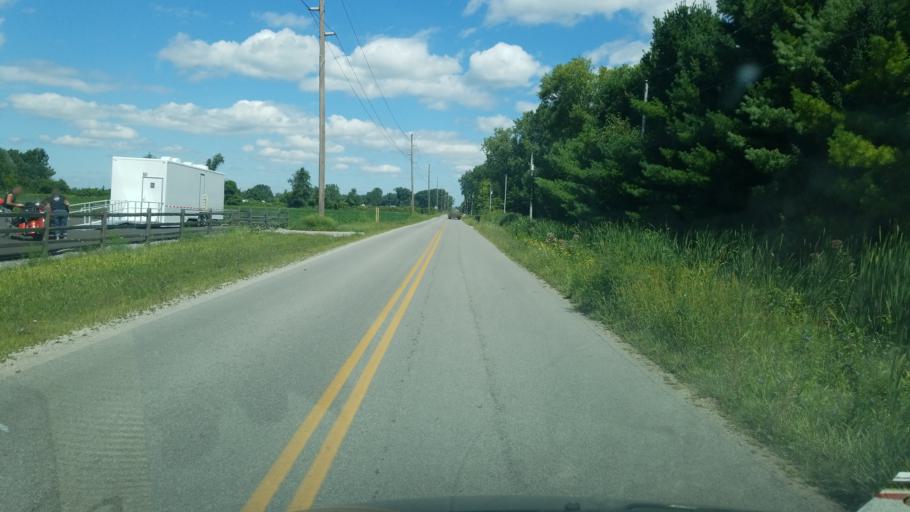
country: US
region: Ohio
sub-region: Henry County
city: Liberty Center
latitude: 41.4513
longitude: -83.9214
